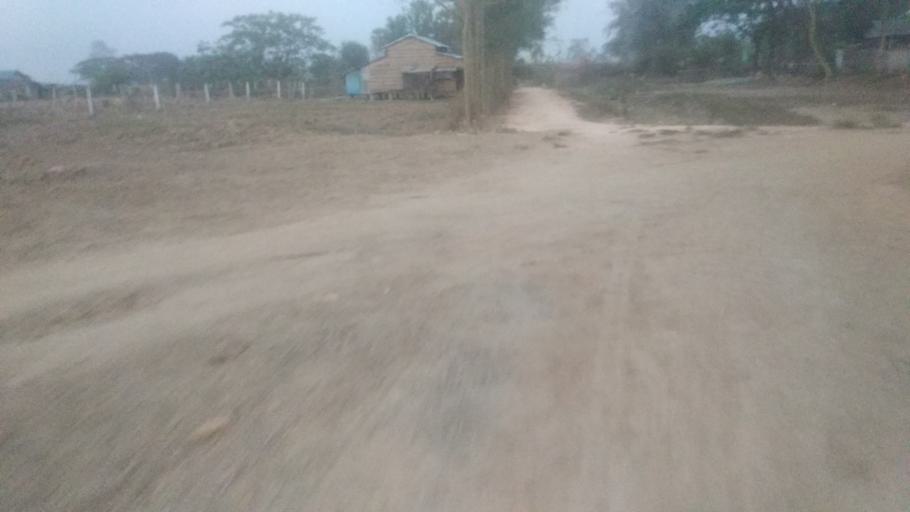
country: MM
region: Yangon
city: Kanbe
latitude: 16.8753
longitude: 95.9804
